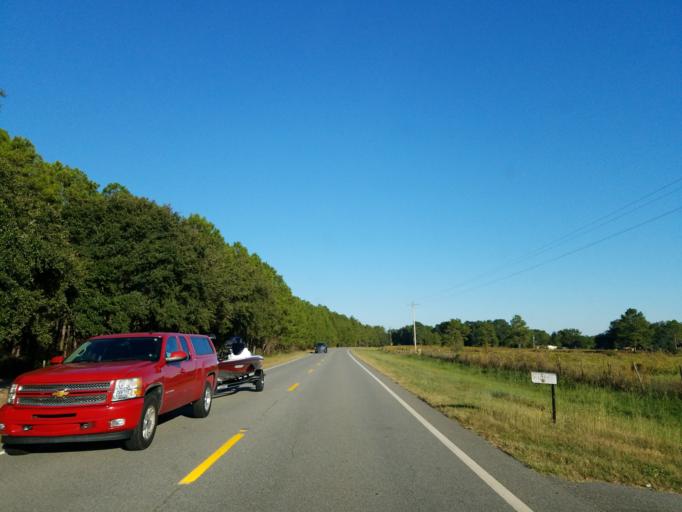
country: US
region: Georgia
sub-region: Lee County
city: Leesburg
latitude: 31.7290
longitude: -84.0626
